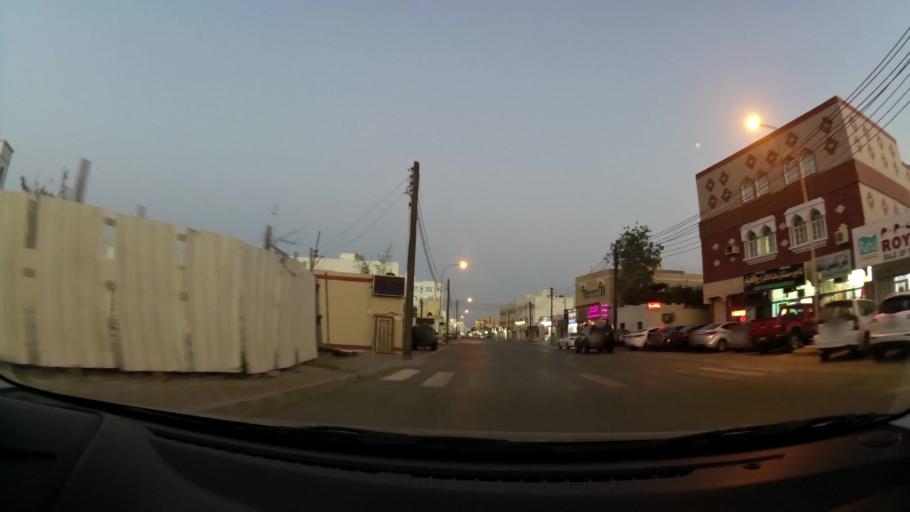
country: OM
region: Muhafazat Masqat
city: As Sib al Jadidah
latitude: 23.6804
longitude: 58.1848
